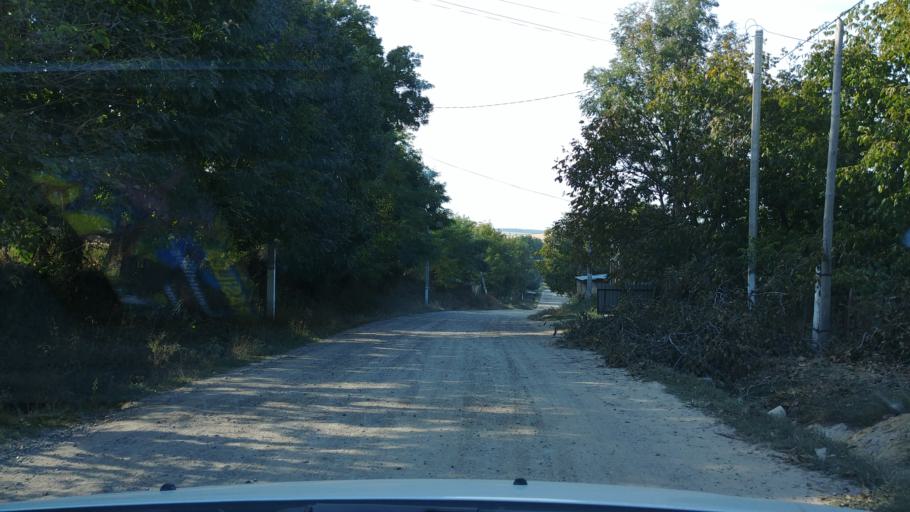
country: MD
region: Rezina
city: Rezina
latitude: 47.7463
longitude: 28.8873
